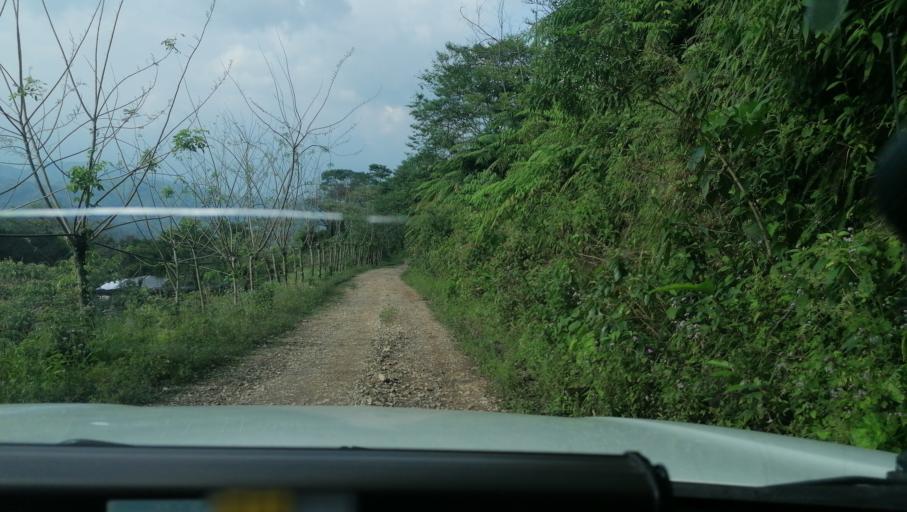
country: MX
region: Chiapas
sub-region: Tapilula
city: San Francisco Jacona
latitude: 17.3178
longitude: -93.0983
